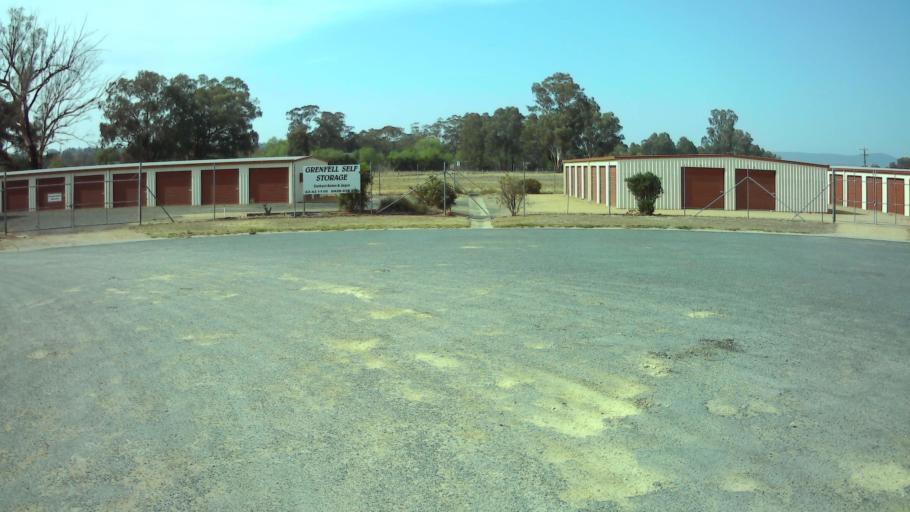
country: AU
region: New South Wales
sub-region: Weddin
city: Grenfell
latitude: -33.9009
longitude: 148.1508
